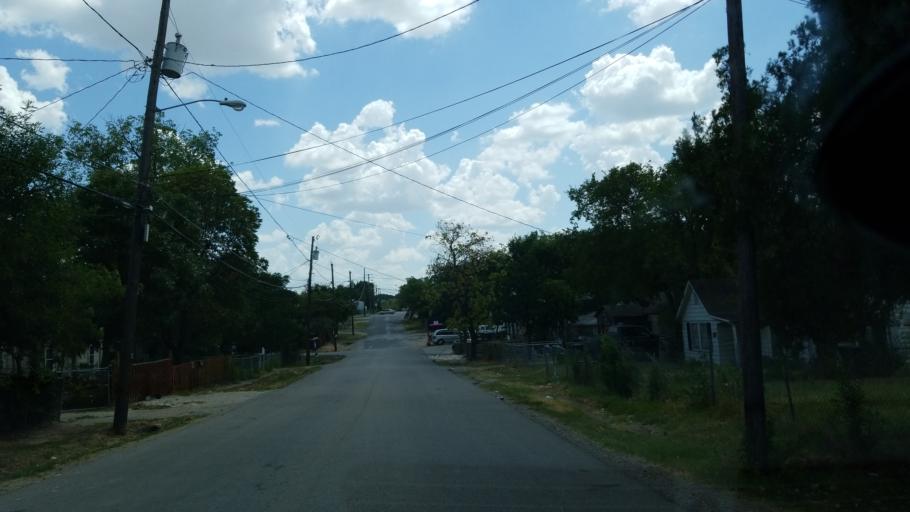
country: US
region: Texas
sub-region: Dallas County
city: Cockrell Hill
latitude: 32.7476
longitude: -96.9115
